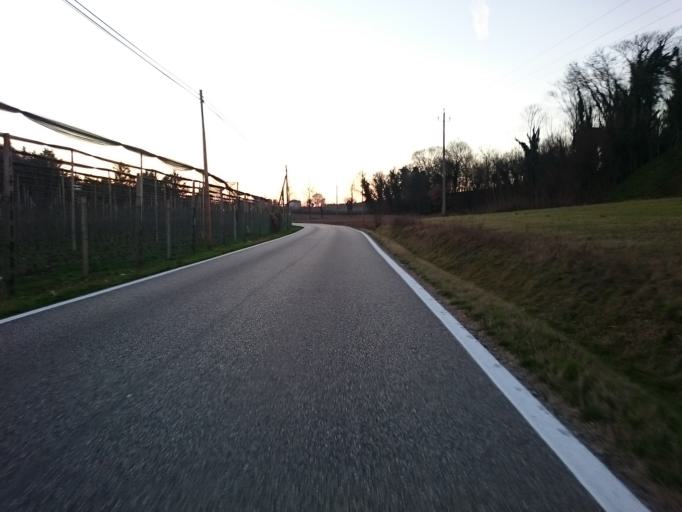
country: IT
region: Veneto
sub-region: Provincia di Verona
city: Salionze
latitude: 45.4075
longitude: 10.7383
